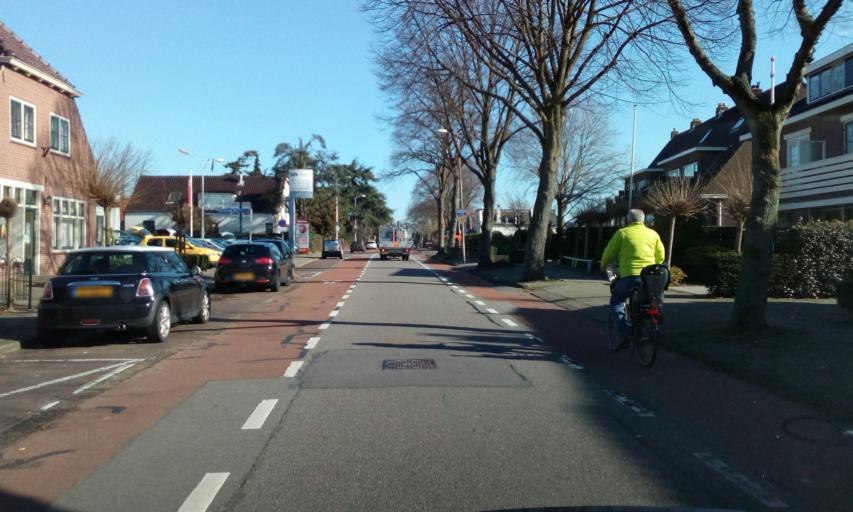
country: NL
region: South Holland
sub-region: Gemeente Zoetermeer
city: Zoetermeer
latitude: 52.0494
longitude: 4.4940
